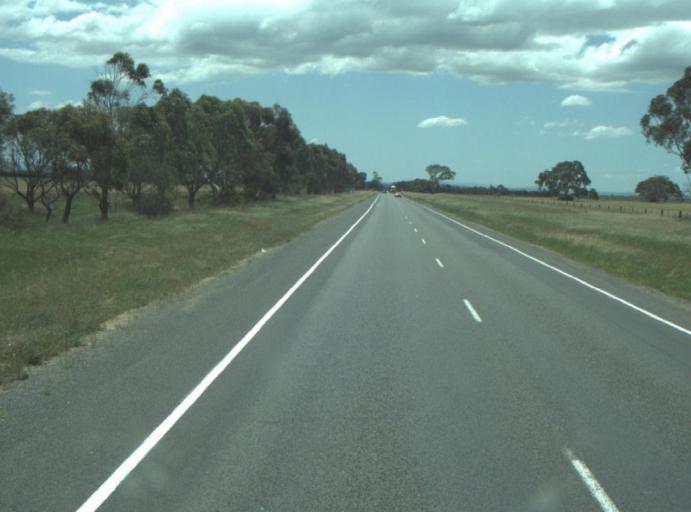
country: AU
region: Victoria
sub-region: Greater Geelong
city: Lara
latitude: -37.8785
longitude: 144.3801
